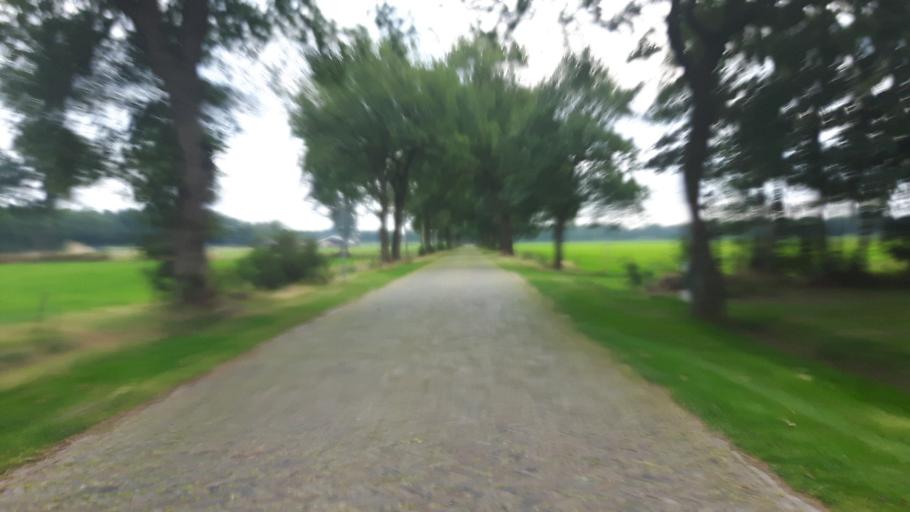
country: NL
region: Friesland
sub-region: Gemeente Heerenveen
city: Jubbega
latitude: 52.9803
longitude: 6.2624
